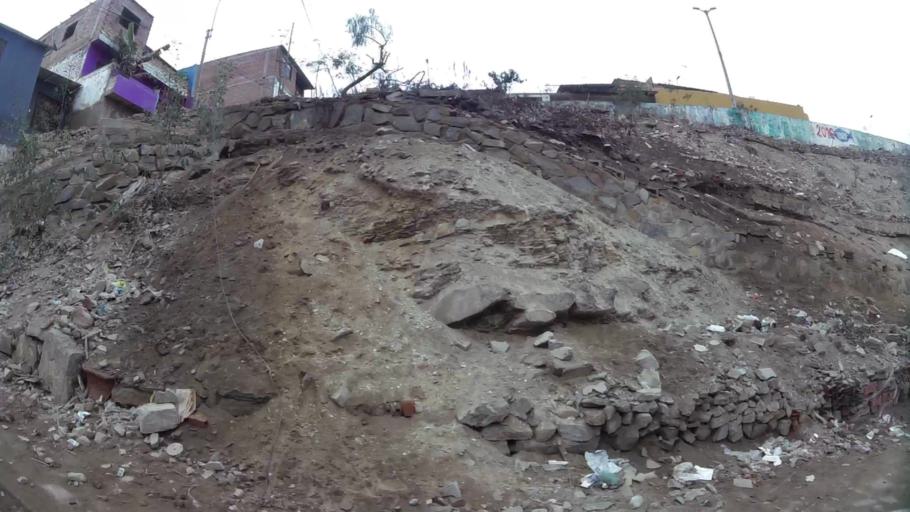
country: PE
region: Lima
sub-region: Lima
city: Surco
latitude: -12.2197
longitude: -76.9197
